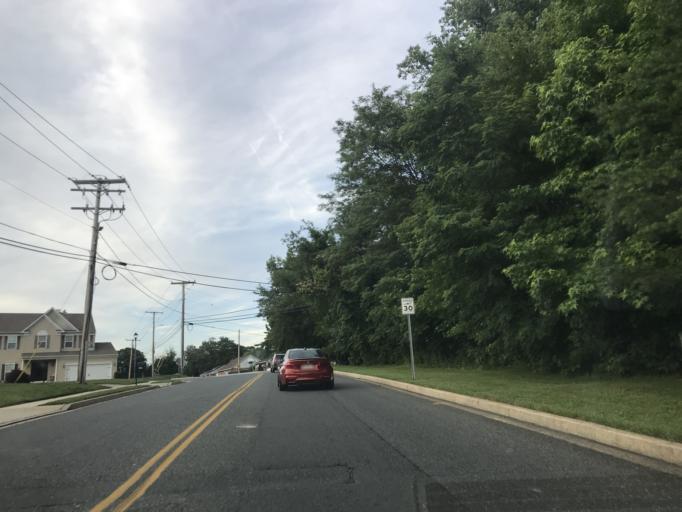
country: US
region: Maryland
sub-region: Harford County
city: Aberdeen
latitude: 39.5150
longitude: -76.1878
